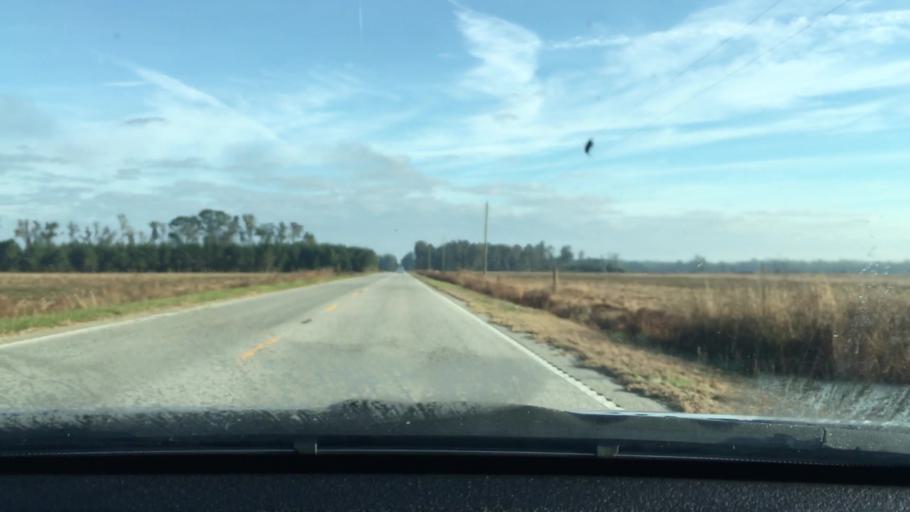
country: US
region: South Carolina
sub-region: Sumter County
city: East Sumter
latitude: 34.0125
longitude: -80.2842
